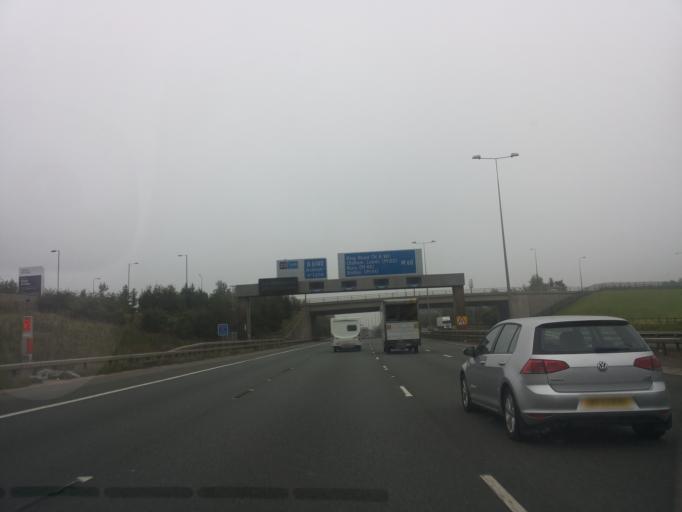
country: GB
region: England
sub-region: Borough of Tameside
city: Droylsden
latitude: 53.4712
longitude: -2.1351
